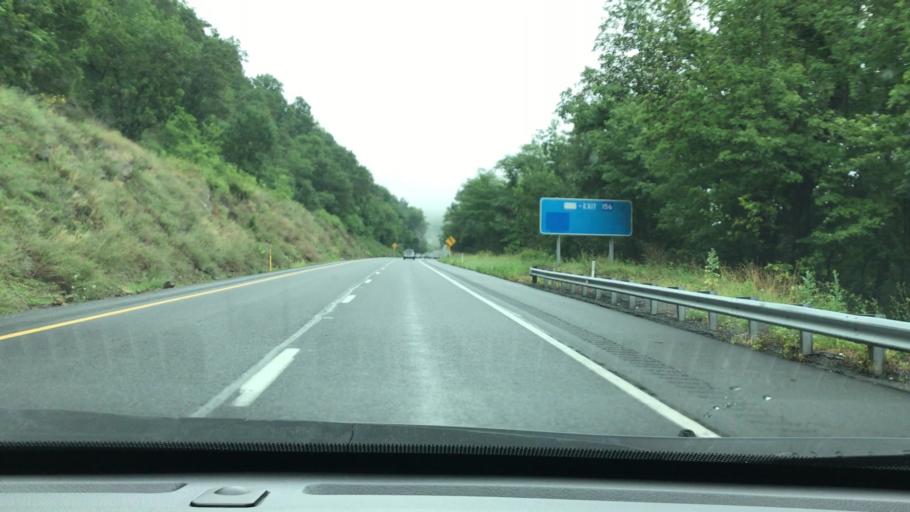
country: US
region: Pennsylvania
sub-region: Bedford County
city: Earlston
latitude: 39.8772
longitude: -78.2478
